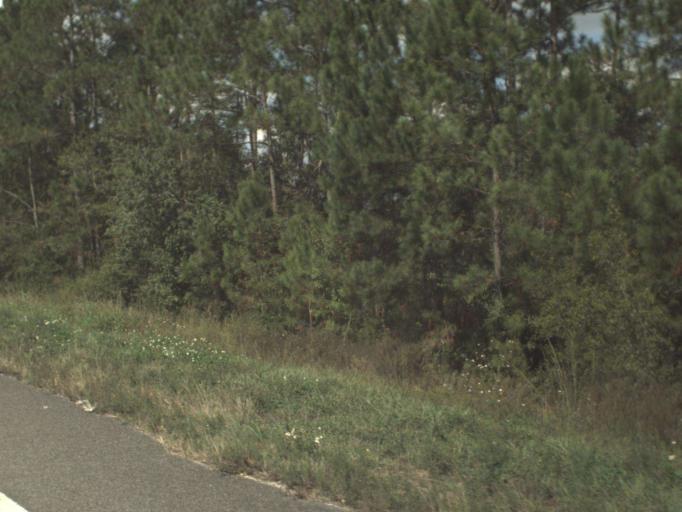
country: US
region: Florida
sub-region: Bay County
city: Laguna Beach
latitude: 30.4537
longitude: -85.9064
